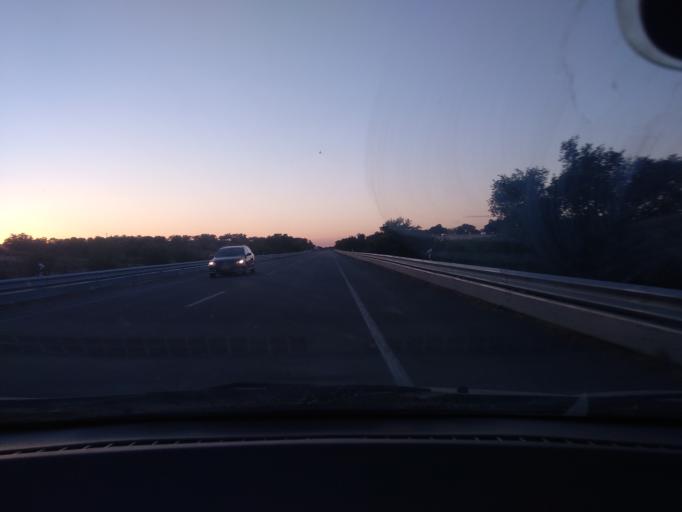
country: PT
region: Beja
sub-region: Beja
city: Beja
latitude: 37.9422
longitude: -7.8751
